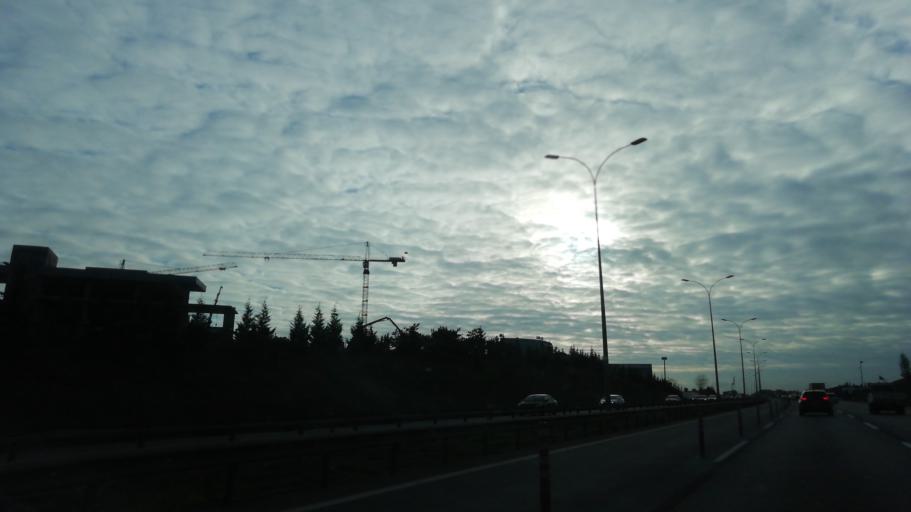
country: TR
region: Kocaeli
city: Balcik
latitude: 40.8880
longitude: 29.3738
